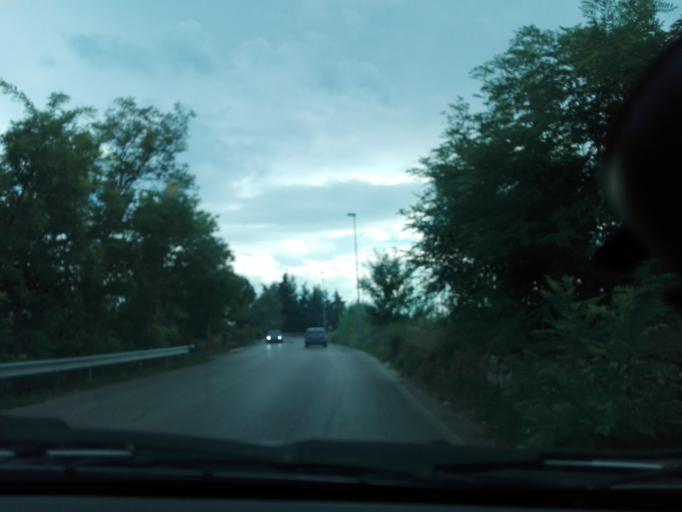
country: IT
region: Abruzzo
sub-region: Provincia di Pescara
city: Cappelle sul Tavo
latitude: 42.4586
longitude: 14.1162
